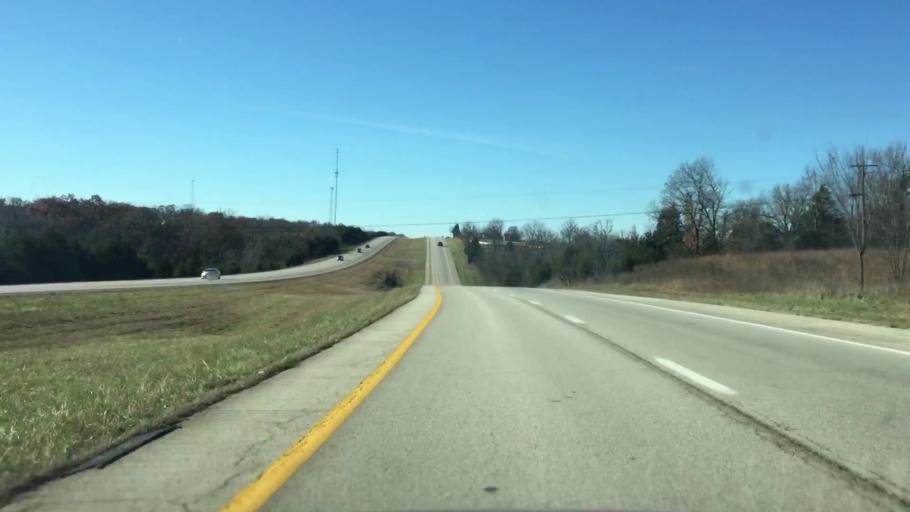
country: US
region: Missouri
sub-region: Cole County
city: Saint Martins
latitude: 38.4207
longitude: -92.3391
